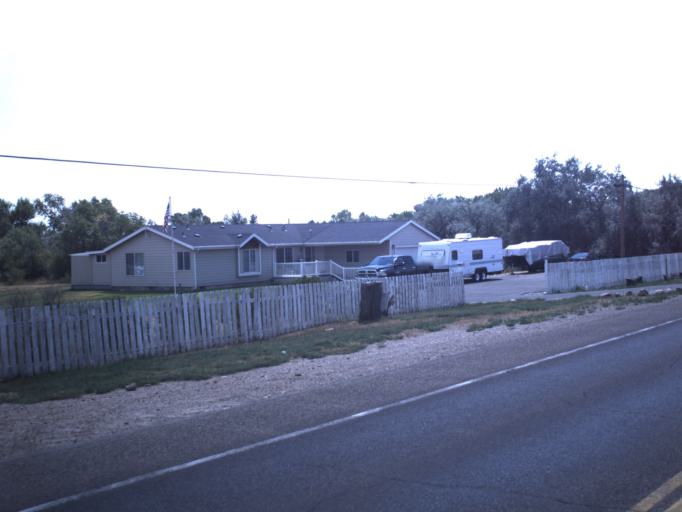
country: US
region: Utah
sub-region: Uintah County
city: Vernal
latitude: 40.4841
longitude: -109.5290
